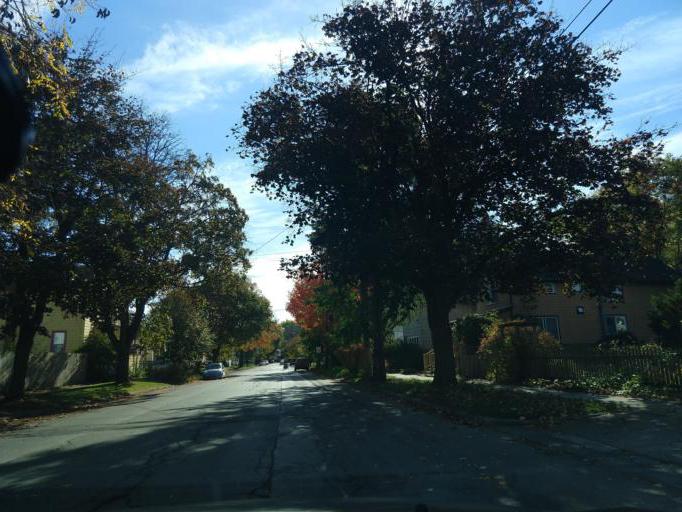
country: US
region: New York
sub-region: Tompkins County
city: Ithaca
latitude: 42.4509
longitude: -76.5028
